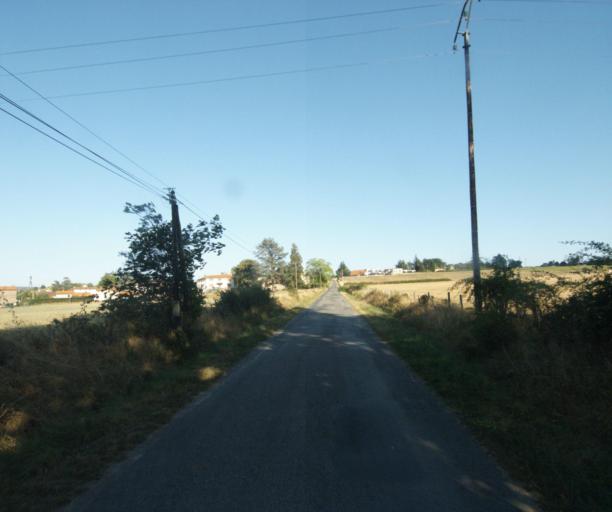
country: FR
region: Rhone-Alpes
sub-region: Departement du Rhone
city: Lentilly
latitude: 45.8299
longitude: 4.6733
